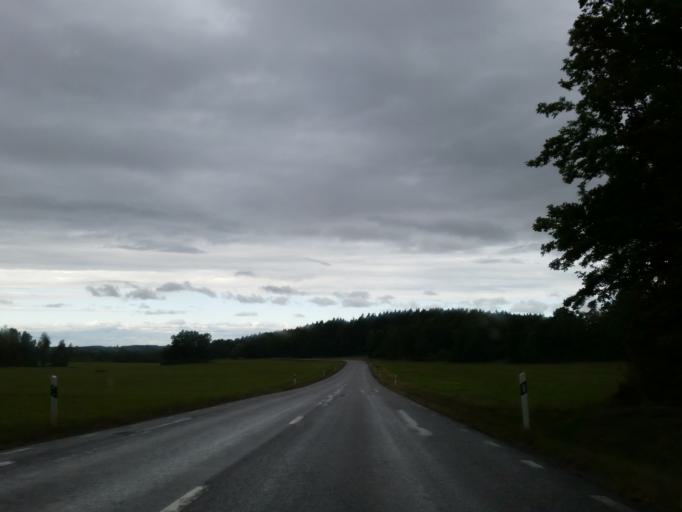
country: SE
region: Uppsala
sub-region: Habo Kommun
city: Balsta
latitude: 59.6473
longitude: 17.4277
